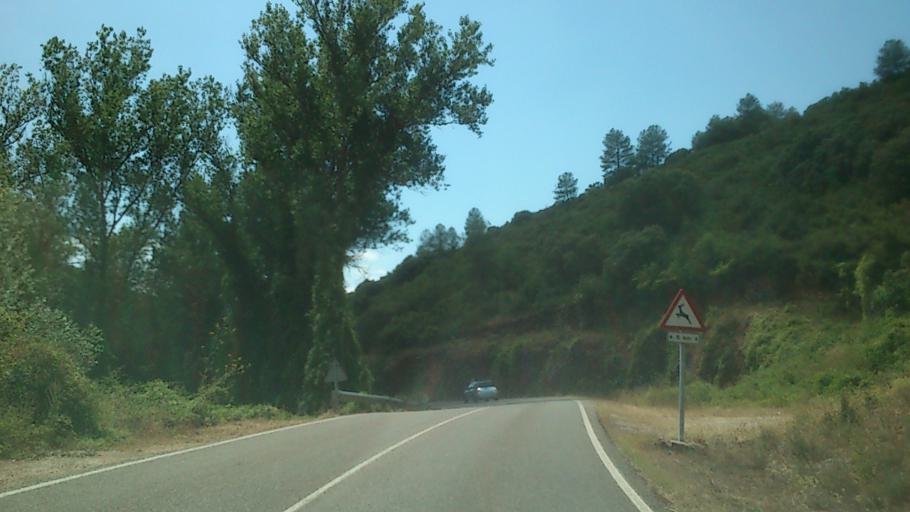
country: ES
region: Castille and Leon
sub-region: Provincia de Burgos
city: Frias
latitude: 42.7585
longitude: -3.2967
